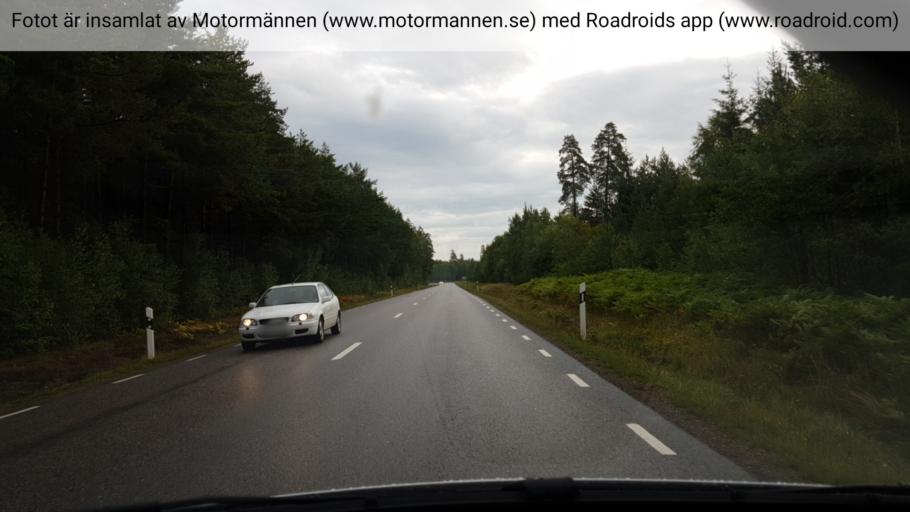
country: SE
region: Vaestra Goetaland
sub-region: Skovde Kommun
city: Stopen
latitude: 58.4492
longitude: 13.9469
